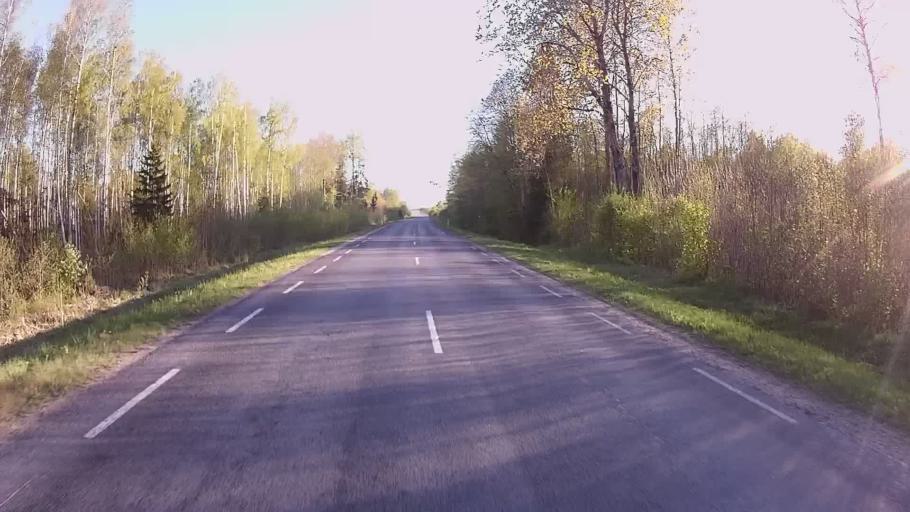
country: EE
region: Viljandimaa
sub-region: Viiratsi vald
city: Viiratsi
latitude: 58.4303
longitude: 25.7175
